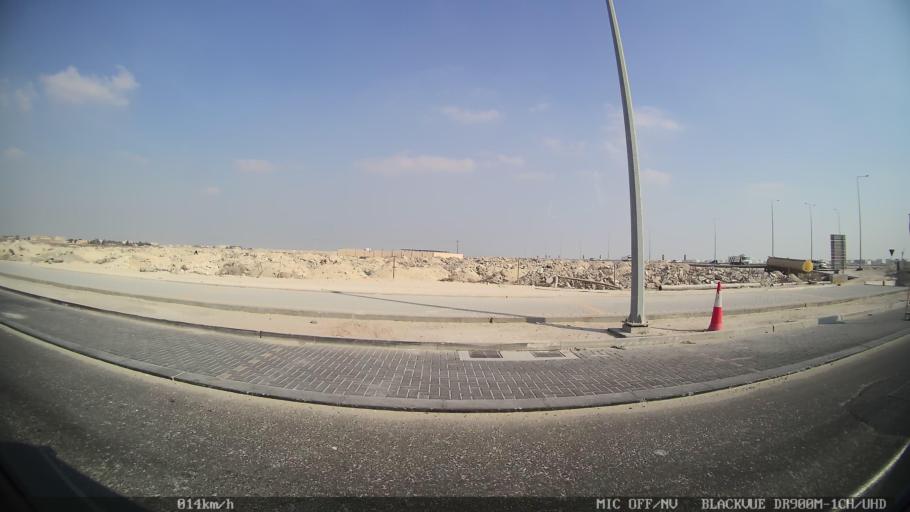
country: QA
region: Al Wakrah
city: Al Wukayr
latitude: 25.1372
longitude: 51.5315
